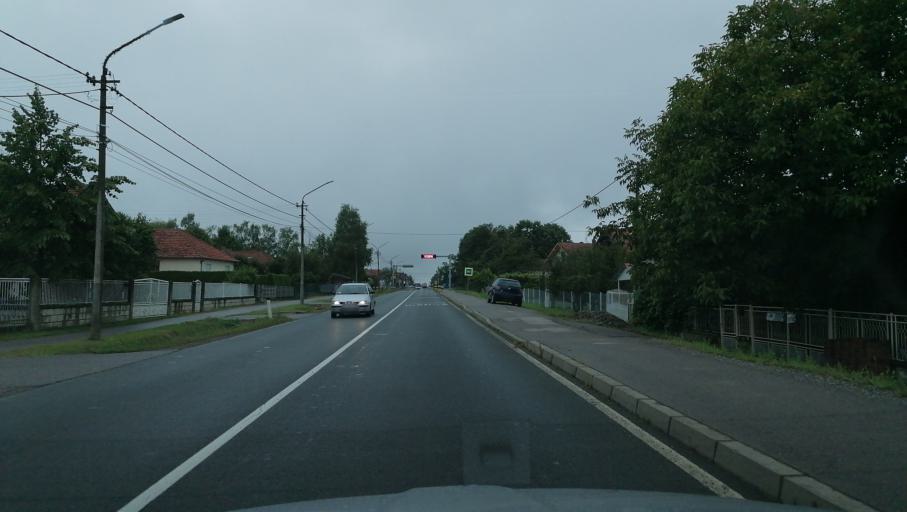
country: RS
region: Central Serbia
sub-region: Rasinski Okrug
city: Krusevac
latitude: 43.5876
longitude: 21.2733
